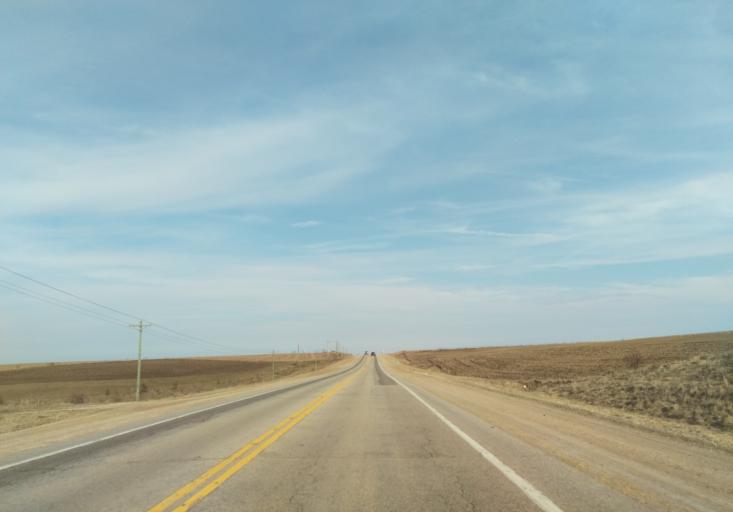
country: US
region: Wisconsin
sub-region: Grant County
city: Lancaster
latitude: 42.9741
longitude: -90.8284
